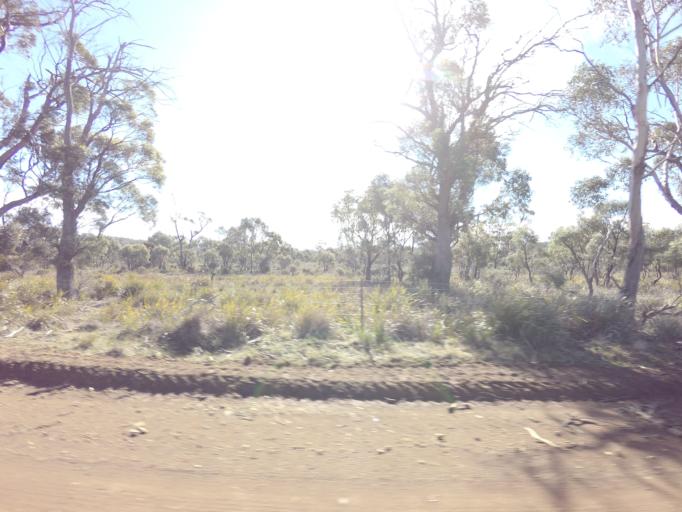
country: AU
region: Tasmania
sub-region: Sorell
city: Sorell
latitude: -42.4161
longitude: 147.9411
